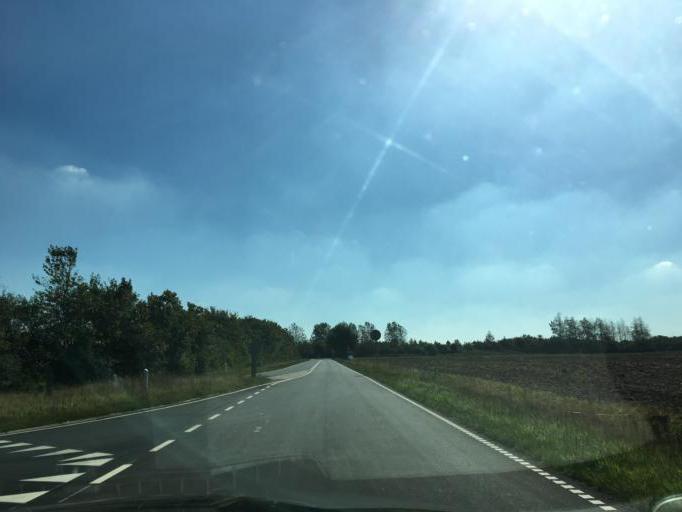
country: DK
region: South Denmark
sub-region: Kolding Kommune
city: Lunderskov
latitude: 55.4949
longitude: 9.2952
